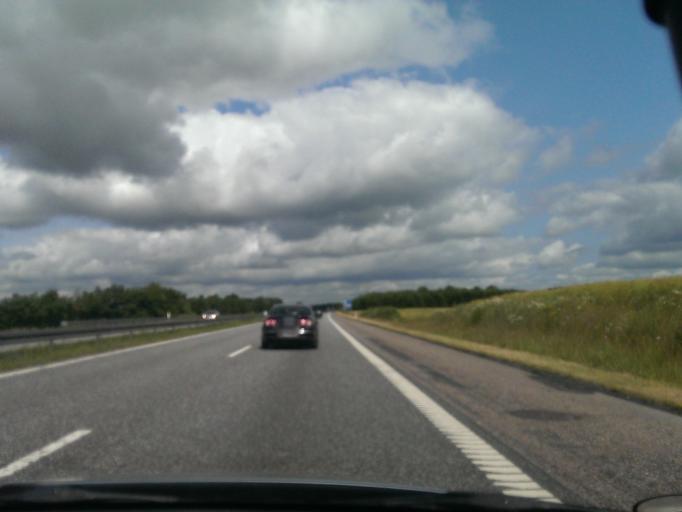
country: DK
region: North Denmark
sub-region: Mariagerfjord Kommune
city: Hobro
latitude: 56.5592
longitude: 9.8672
